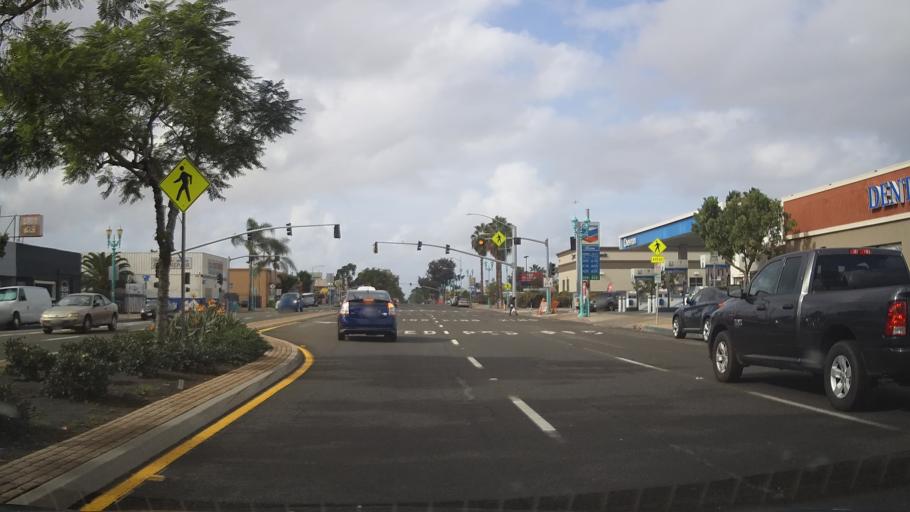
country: US
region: California
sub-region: San Diego County
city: San Diego
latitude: 32.7553
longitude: -117.1150
